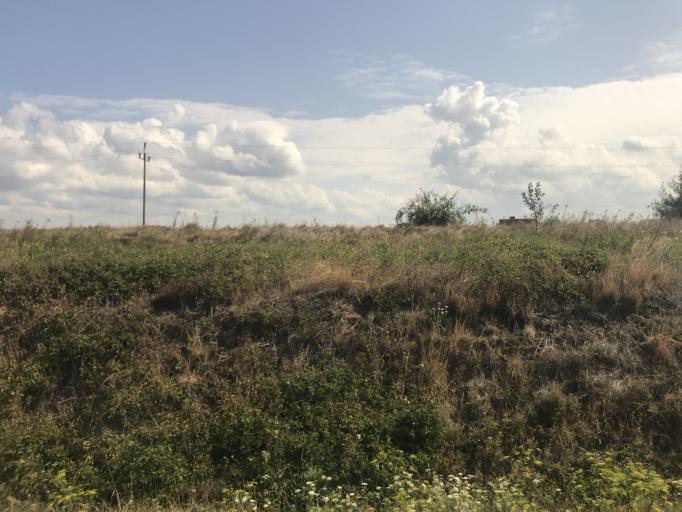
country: PL
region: Kujawsko-Pomorskie
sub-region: Powiat inowroclawski
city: Zlotniki Kujawskie
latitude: 52.9188
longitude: 18.1308
